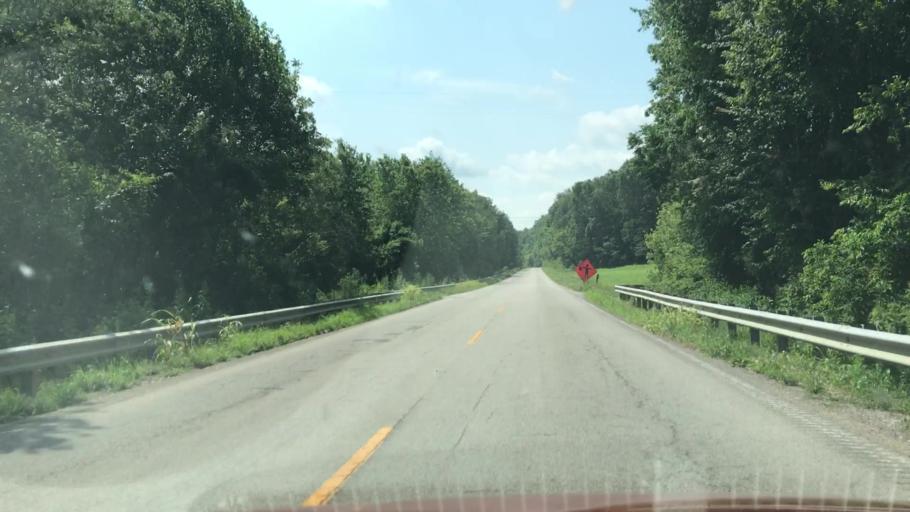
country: US
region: Kentucky
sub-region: Barren County
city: Glasgow
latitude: 36.8646
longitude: -85.8472
